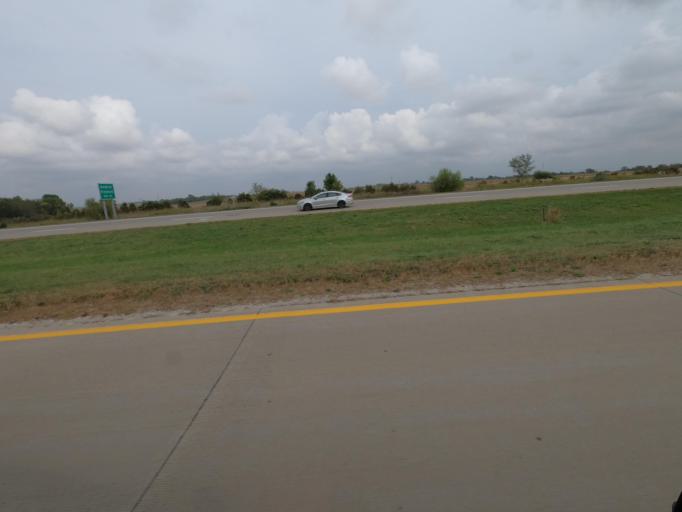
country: US
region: Iowa
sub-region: Wapello County
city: Ottumwa
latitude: 41.0853
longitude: -92.3942
